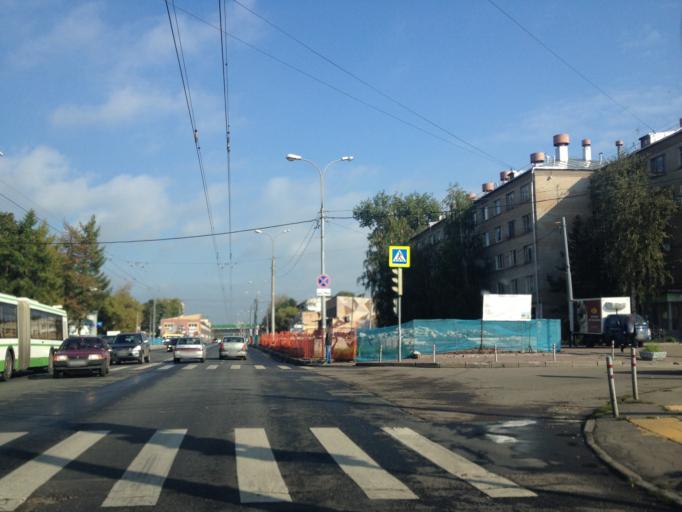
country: RU
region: Moscow
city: Metrogorodok
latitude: 55.8064
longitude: 37.7988
